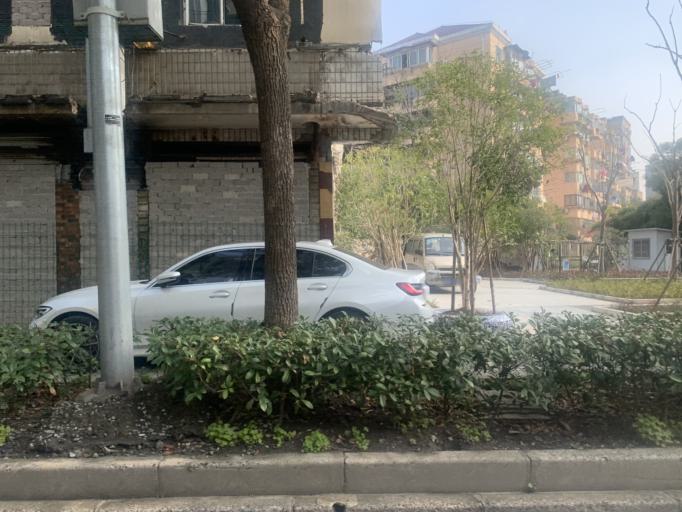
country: CN
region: Shanghai Shi
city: Huamu
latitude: 31.1837
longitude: 121.5154
